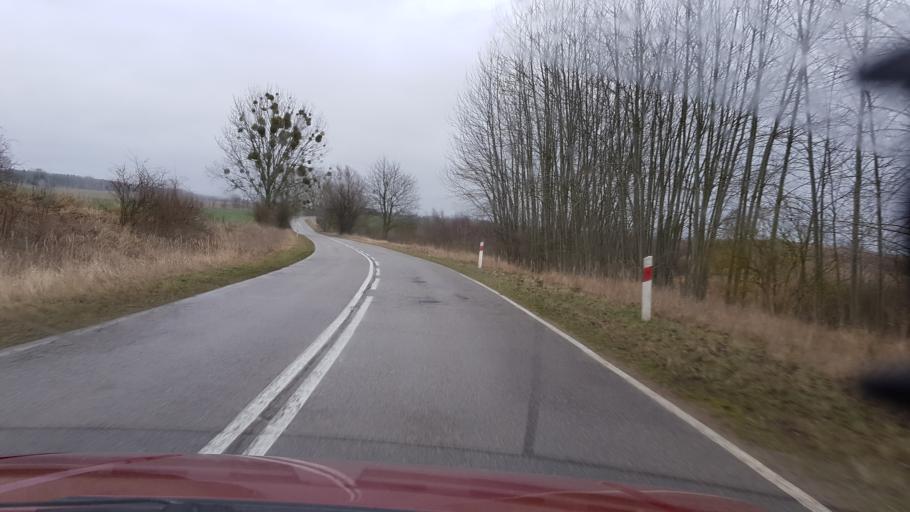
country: PL
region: West Pomeranian Voivodeship
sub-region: Powiat gryfinski
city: Gryfino
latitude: 53.3174
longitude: 14.5810
